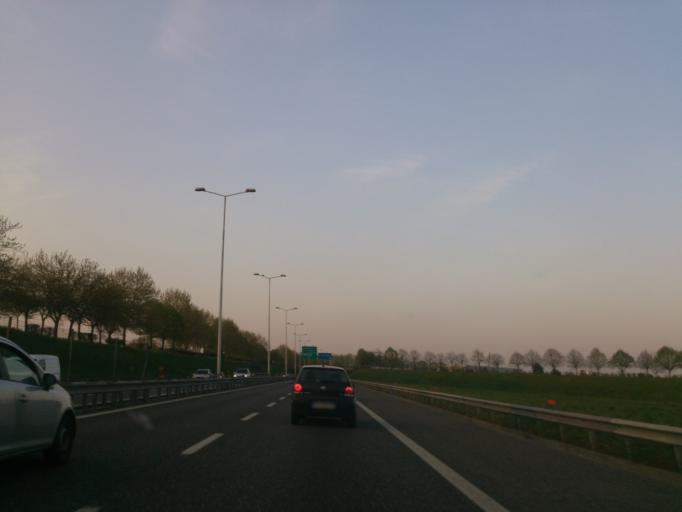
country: IT
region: Lombardy
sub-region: Provincia di Monza e Brianza
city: Nova Milanese
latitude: 45.5719
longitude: 9.2000
